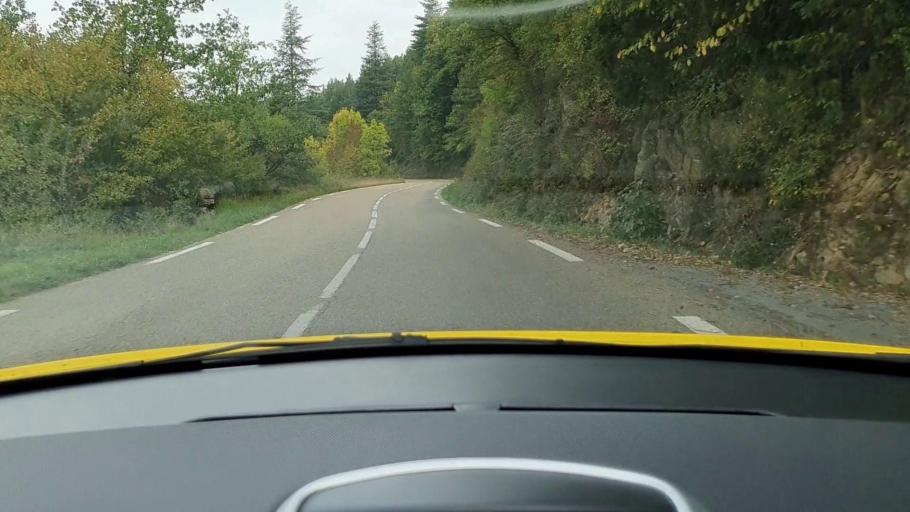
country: FR
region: Languedoc-Roussillon
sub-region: Departement du Gard
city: Le Vigan
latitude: 43.9880
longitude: 3.5890
